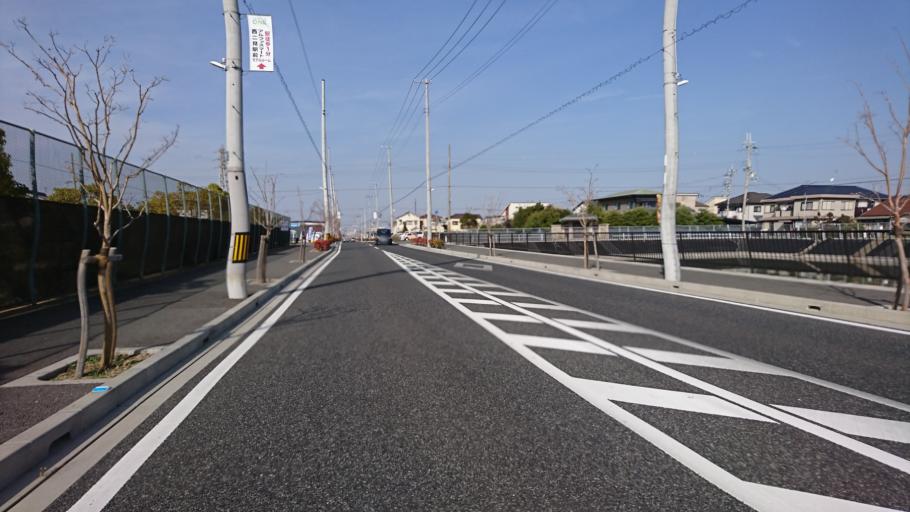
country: JP
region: Hyogo
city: Kakogawacho-honmachi
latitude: 34.7072
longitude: 134.8740
